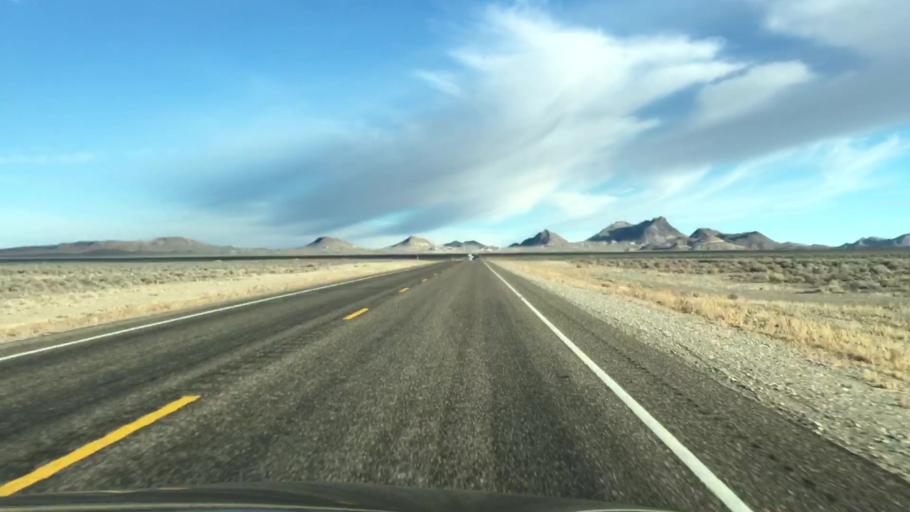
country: US
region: Nevada
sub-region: Nye County
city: Tonopah
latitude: 38.0998
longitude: -117.3277
